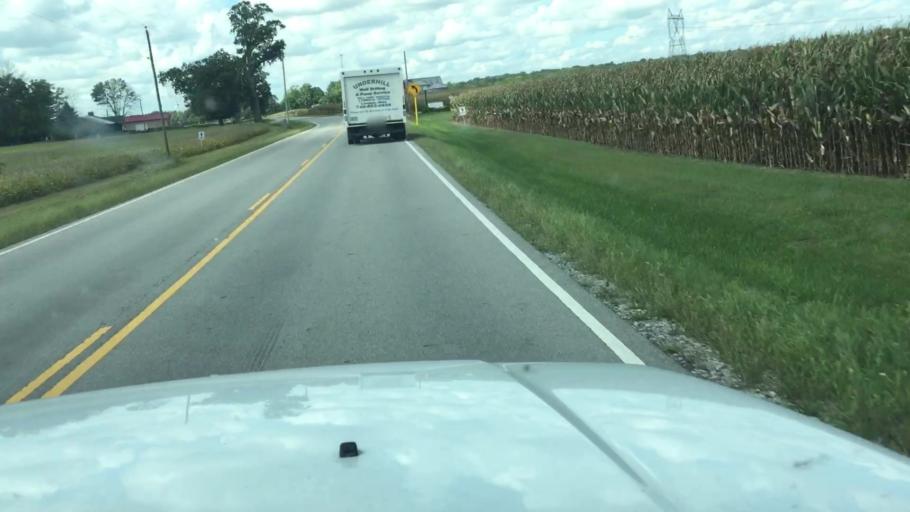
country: US
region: Ohio
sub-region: Madison County
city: Bethel
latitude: 39.8079
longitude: -83.3381
